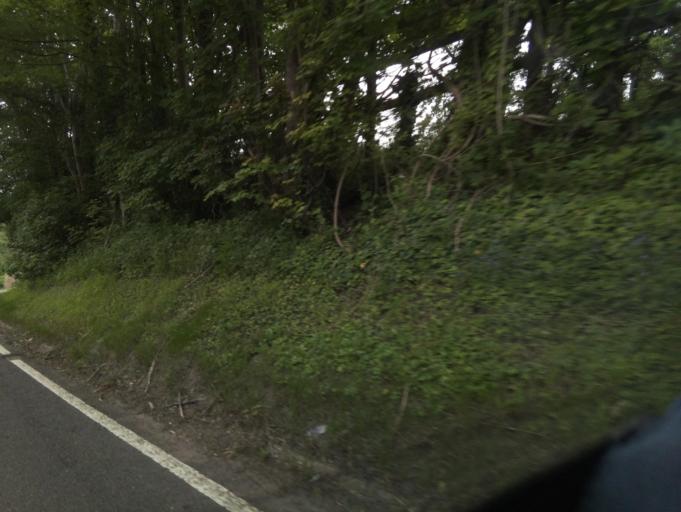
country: GB
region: England
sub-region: Herefordshire
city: Yatton
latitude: 51.9858
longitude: -2.5064
